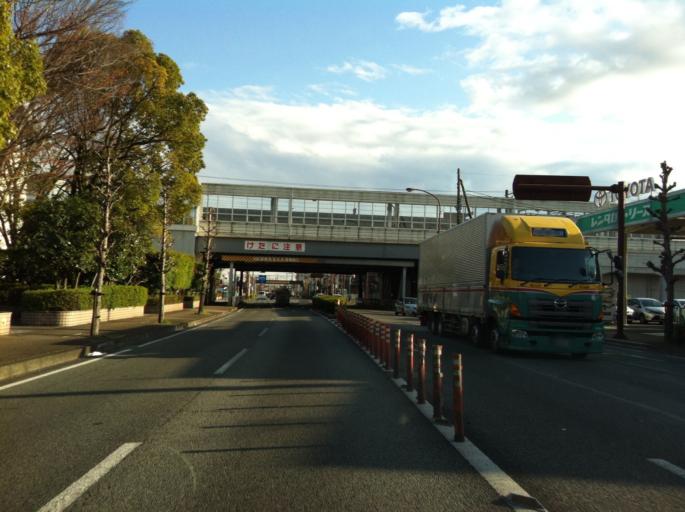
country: JP
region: Shizuoka
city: Fuji
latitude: 35.1428
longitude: 138.6622
